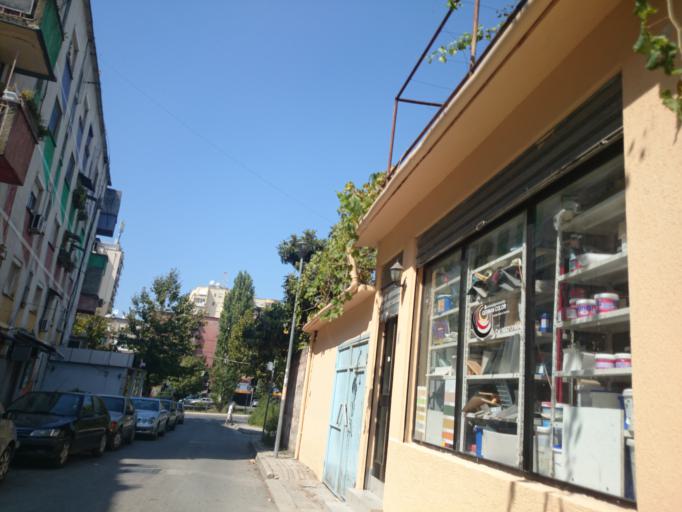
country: AL
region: Tirane
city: Tirana
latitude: 41.3294
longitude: 19.8339
